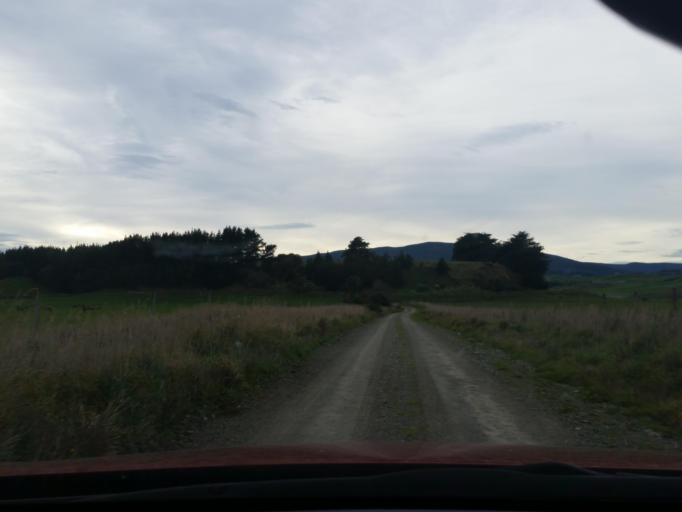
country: NZ
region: Southland
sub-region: Southland District
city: Riverton
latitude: -46.1834
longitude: 167.6735
